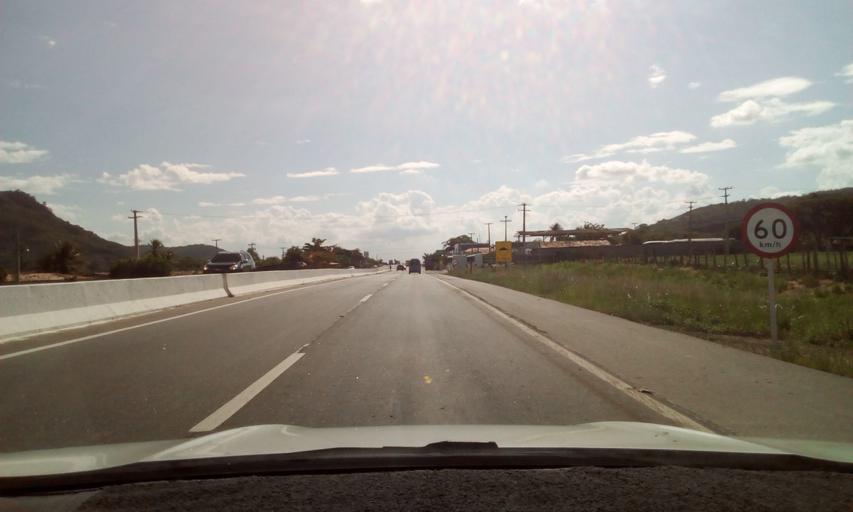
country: BR
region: Paraiba
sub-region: Gurinhem
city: Gurinhem
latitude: -7.1722
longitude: -35.3899
